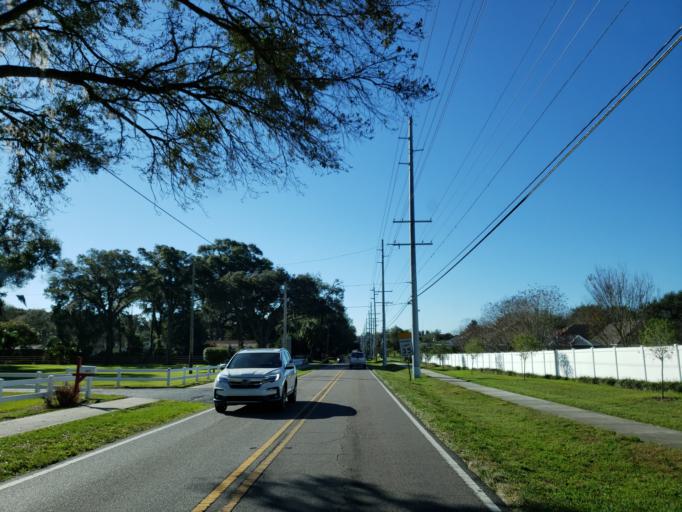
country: US
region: Florida
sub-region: Hillsborough County
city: Bloomingdale
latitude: 27.9001
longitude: -82.2279
